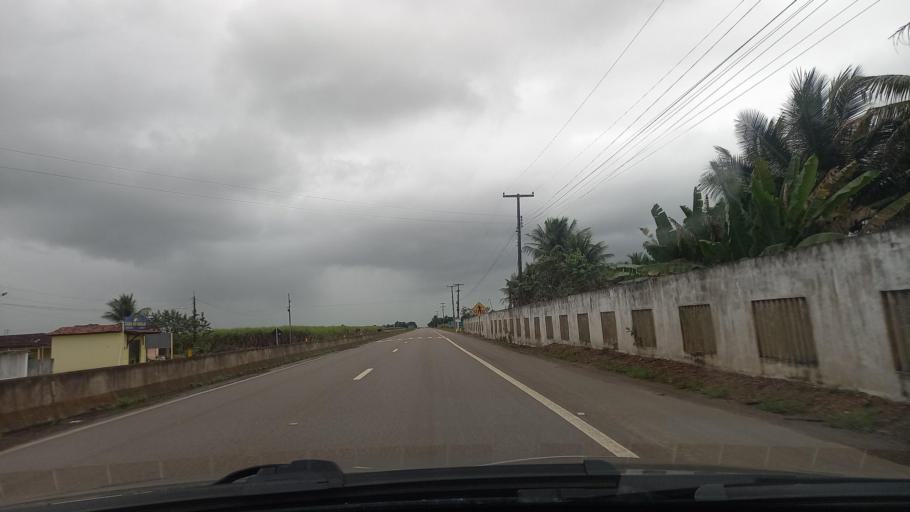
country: BR
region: Alagoas
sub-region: Limoeiro De Anadia
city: Cajueiro
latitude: -9.7606
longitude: -36.4368
